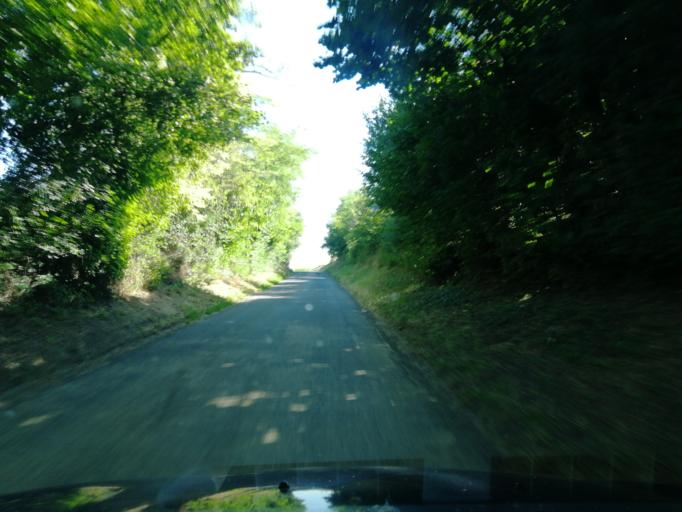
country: FR
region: Rhone-Alpes
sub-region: Departement du Rhone
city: Sathonay-Village
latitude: 45.8441
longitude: 4.8933
